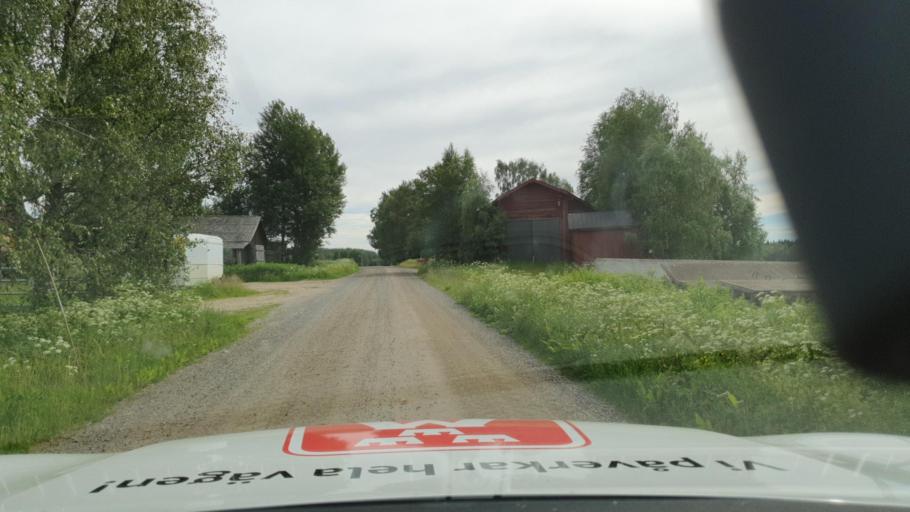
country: SE
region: Vaesterbotten
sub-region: Robertsfors Kommun
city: Robertsfors
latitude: 64.3826
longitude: 21.0360
